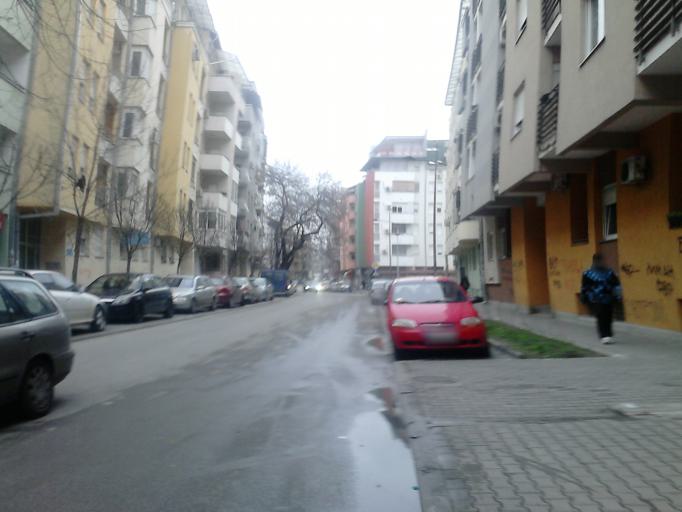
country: RS
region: Autonomna Pokrajina Vojvodina
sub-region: Juznobacki Okrug
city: Novi Sad
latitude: 45.2465
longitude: 19.8339
